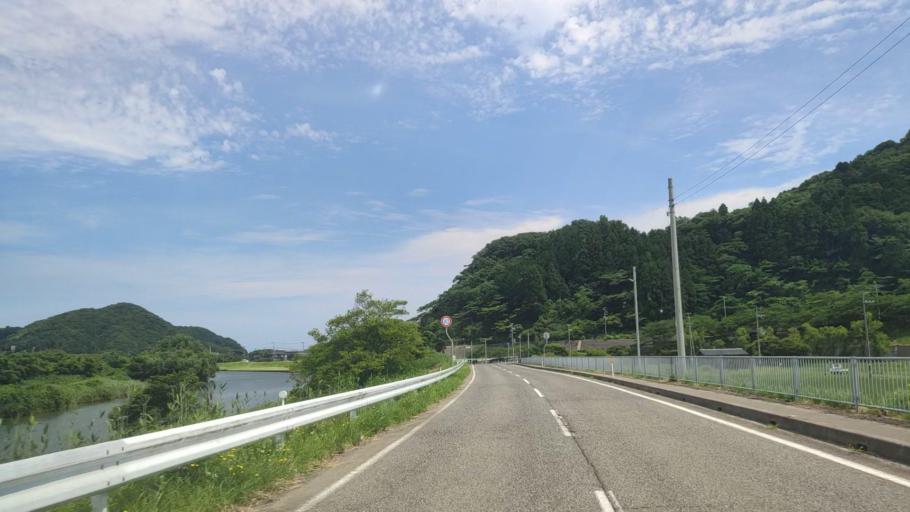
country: JP
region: Hyogo
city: Toyooka
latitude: 35.6502
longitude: 134.7638
